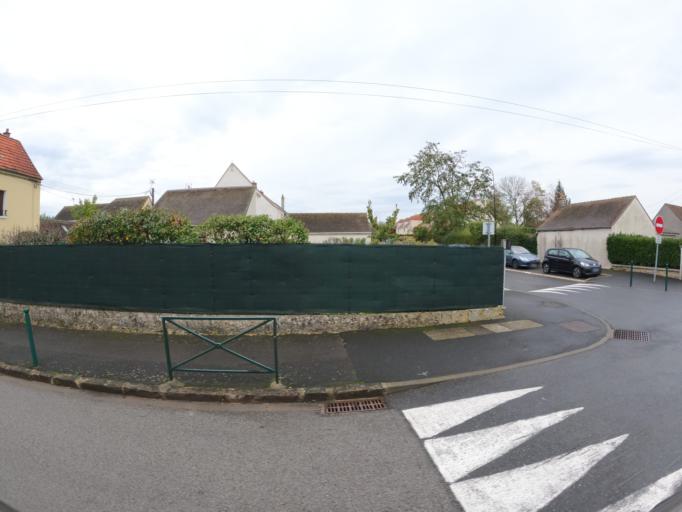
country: FR
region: Ile-de-France
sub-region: Departement de Seine-et-Marne
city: Villeneuve-le-Comte
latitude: 48.8162
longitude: 2.8305
